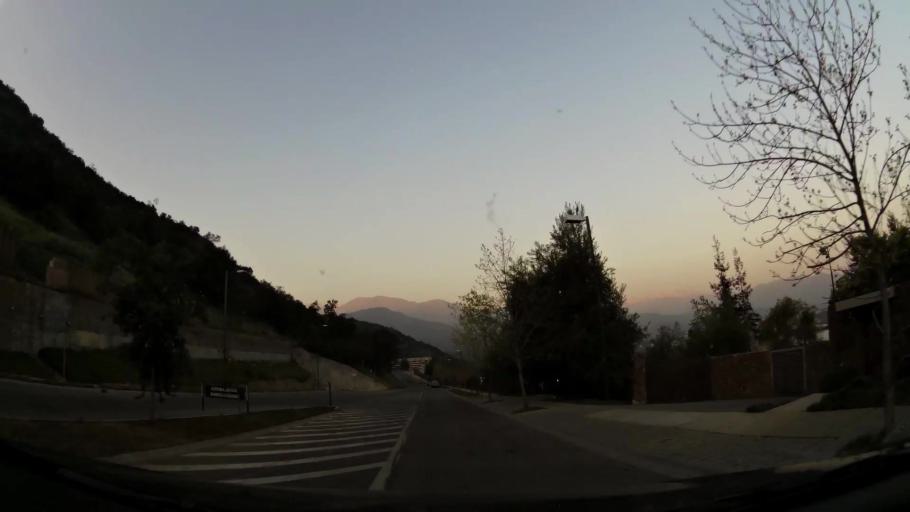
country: CL
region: Santiago Metropolitan
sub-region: Provincia de Chacabuco
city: Chicureo Abajo
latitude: -33.3348
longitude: -70.5584
